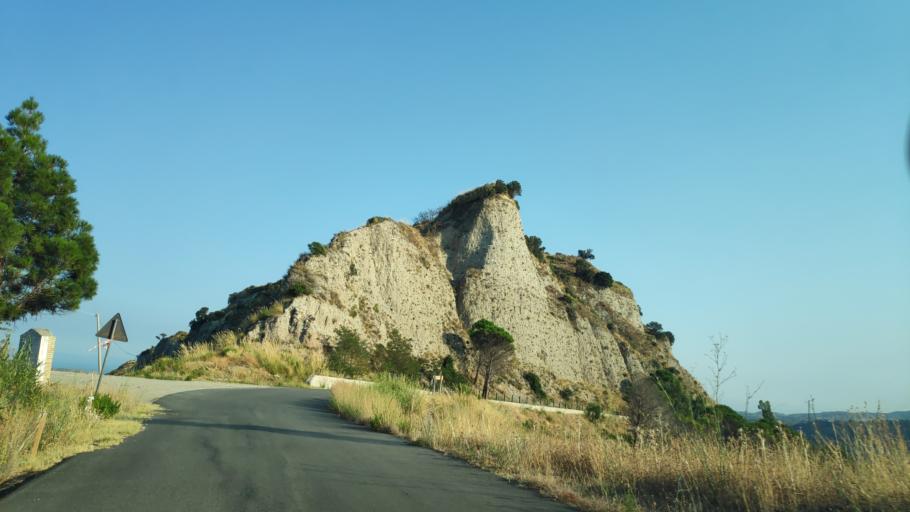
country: IT
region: Calabria
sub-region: Provincia di Reggio Calabria
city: Placanica
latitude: 38.4047
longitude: 16.4285
